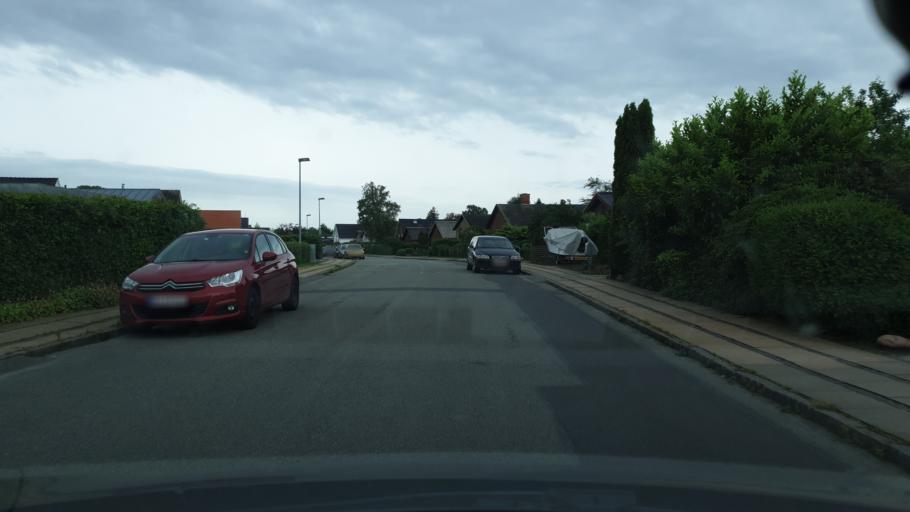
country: DK
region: South Denmark
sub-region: Kolding Kommune
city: Kolding
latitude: 55.5017
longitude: 9.4956
